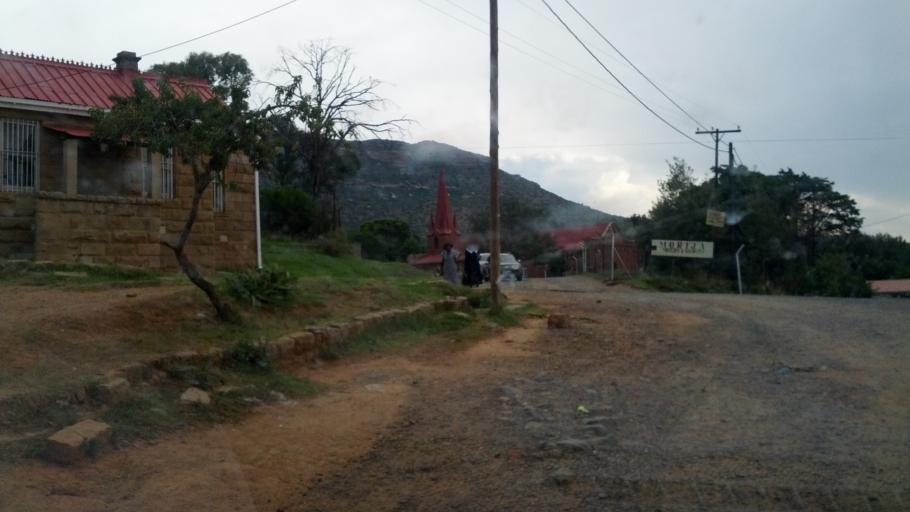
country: LS
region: Maseru
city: Nako
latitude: -29.6244
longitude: 27.5091
